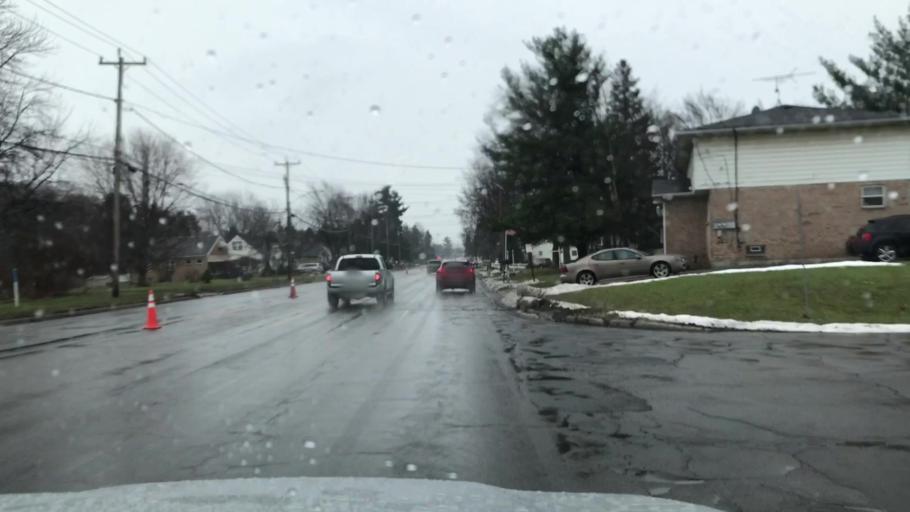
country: US
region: New York
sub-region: Erie County
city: Blasdell
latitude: 42.7886
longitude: -78.7918
